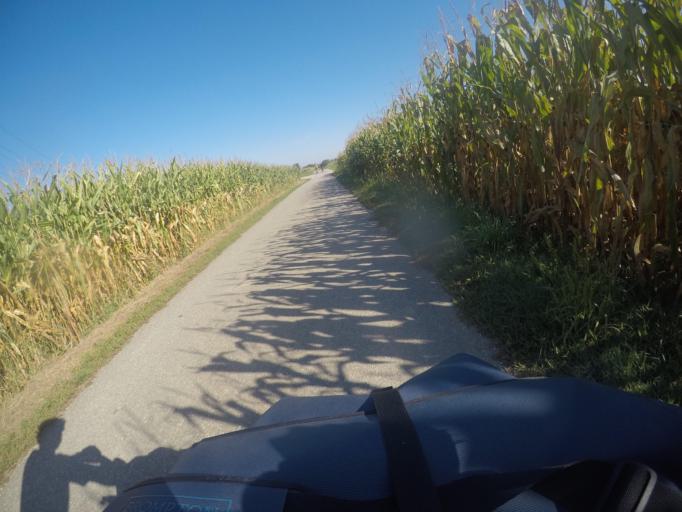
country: FR
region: Alsace
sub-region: Departement du Haut-Rhin
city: Ottmarsheim
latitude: 47.7739
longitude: 7.5056
